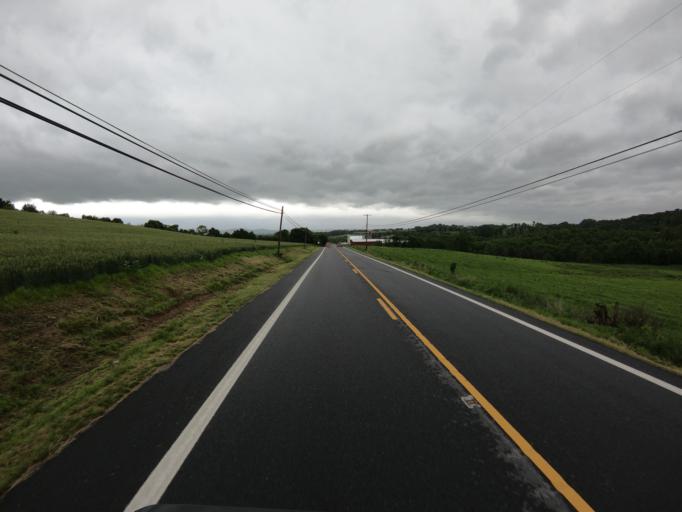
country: US
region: Maryland
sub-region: Frederick County
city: Myersville
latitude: 39.4742
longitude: -77.6044
